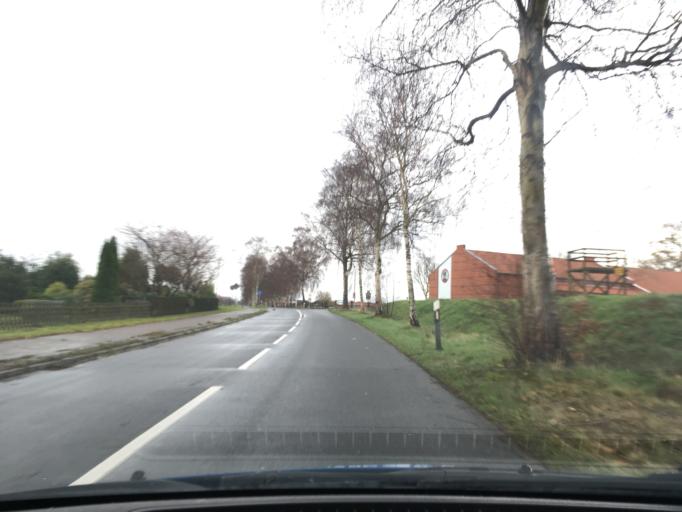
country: DE
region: Lower Saxony
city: Embsen
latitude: 53.1794
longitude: 10.3403
